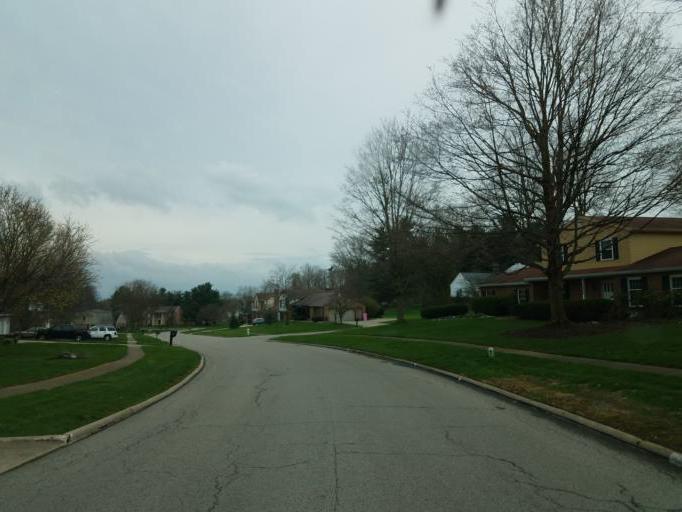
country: US
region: Ohio
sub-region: Richland County
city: Lexington
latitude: 40.7198
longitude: -82.5573
